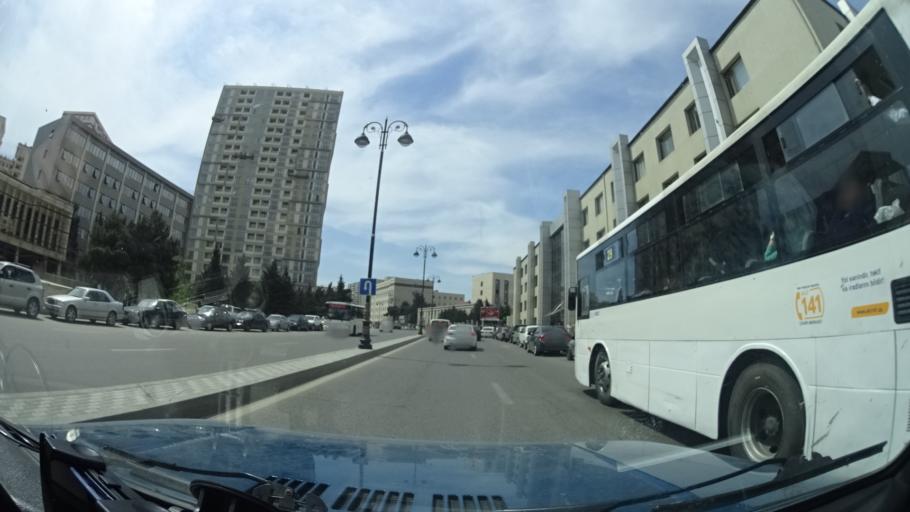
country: AZ
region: Baki
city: Khodzhi-Gasan
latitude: 40.4023
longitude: 49.8065
